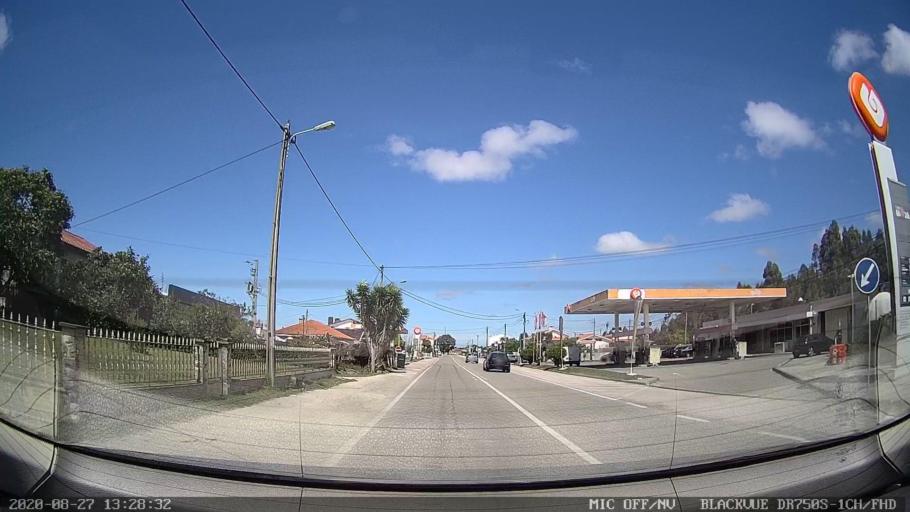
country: PT
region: Aveiro
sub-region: Vagos
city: Vagos
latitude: 40.5191
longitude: -8.6789
